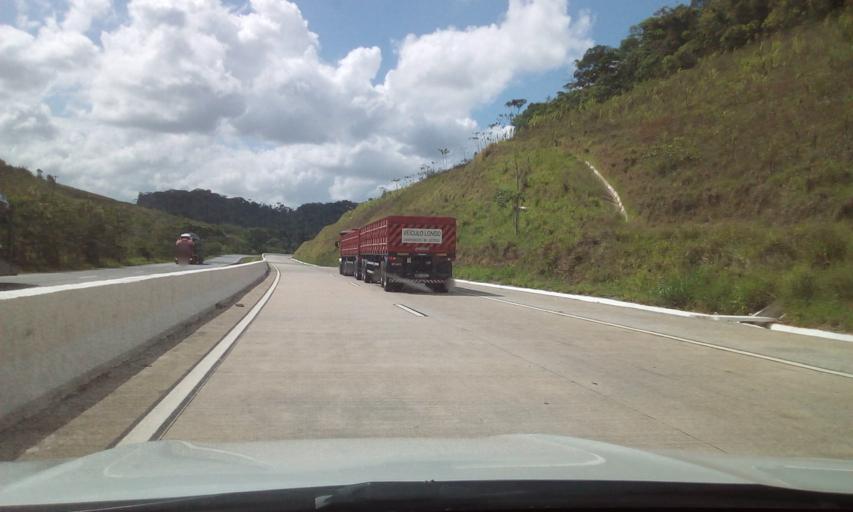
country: BR
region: Pernambuco
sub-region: Palmares
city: Palmares
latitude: -8.7518
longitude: -35.6028
